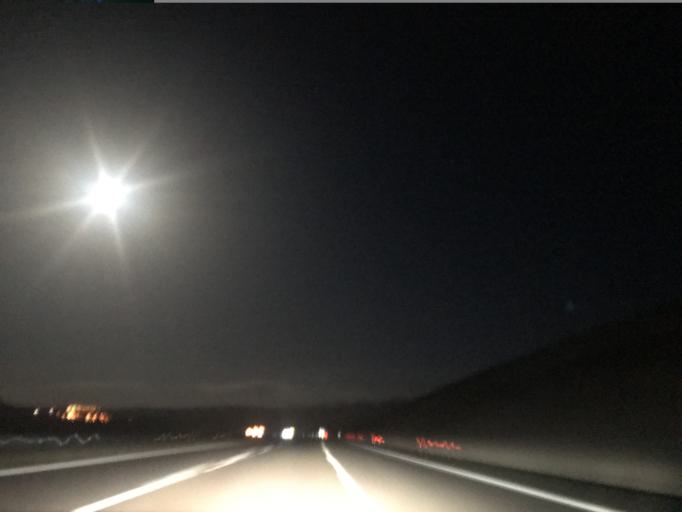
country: TR
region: Nigde
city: Ulukisla
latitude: 37.6341
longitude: 34.4479
